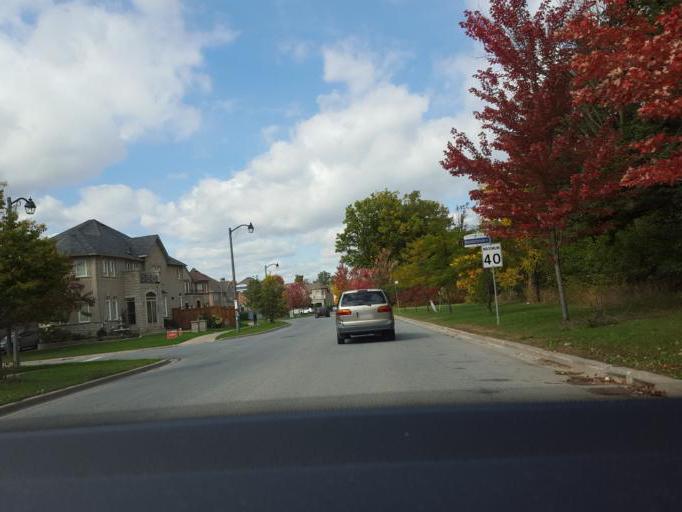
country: CA
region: Ontario
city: Markham
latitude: 43.8327
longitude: -79.2246
